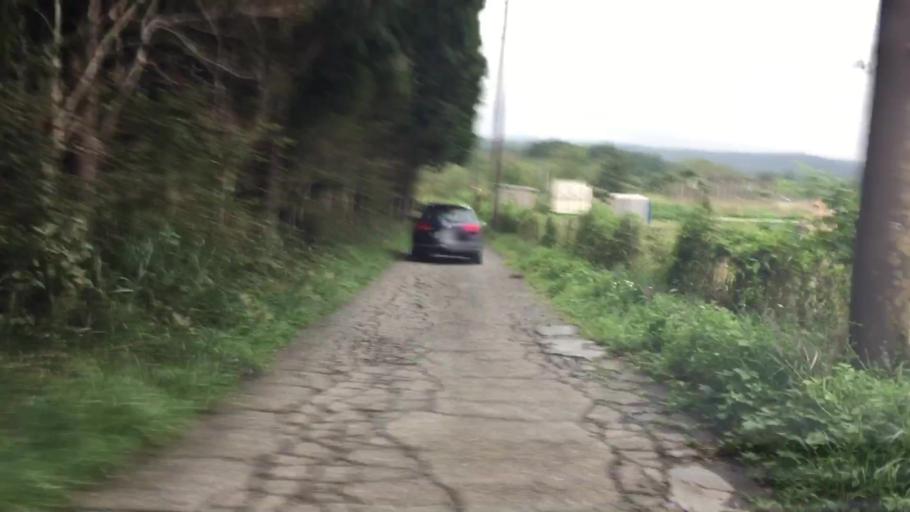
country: JP
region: Yamanashi
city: Fujikawaguchiko
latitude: 35.4023
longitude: 138.5645
